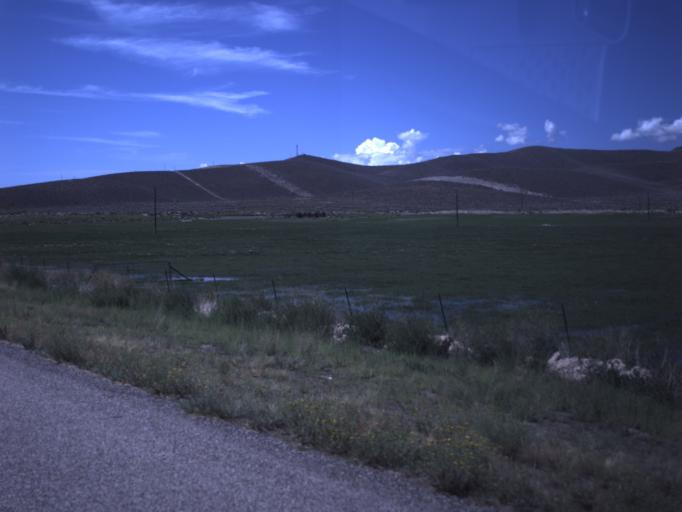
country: US
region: Utah
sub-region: Piute County
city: Junction
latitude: 38.2283
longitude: -112.2198
